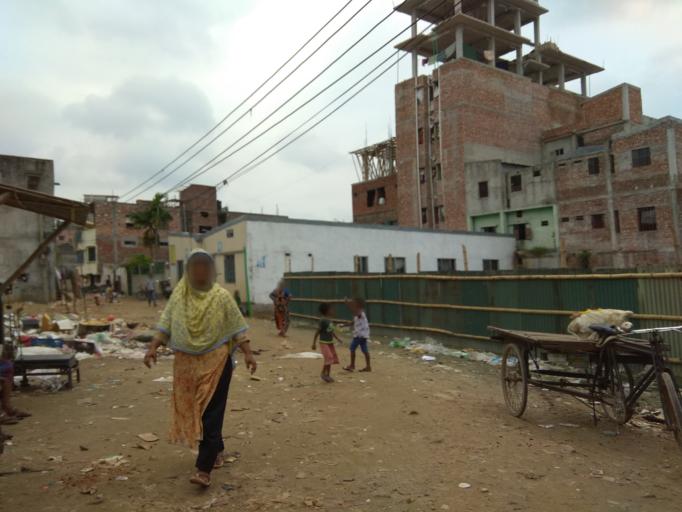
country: BD
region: Dhaka
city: Tungi
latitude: 23.8141
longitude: 90.3771
